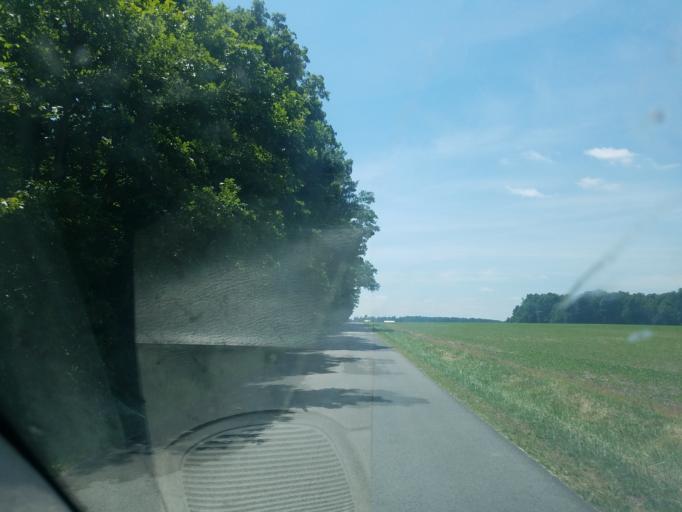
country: US
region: Ohio
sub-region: Hancock County
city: Arlington
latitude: 40.8598
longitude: -83.7084
